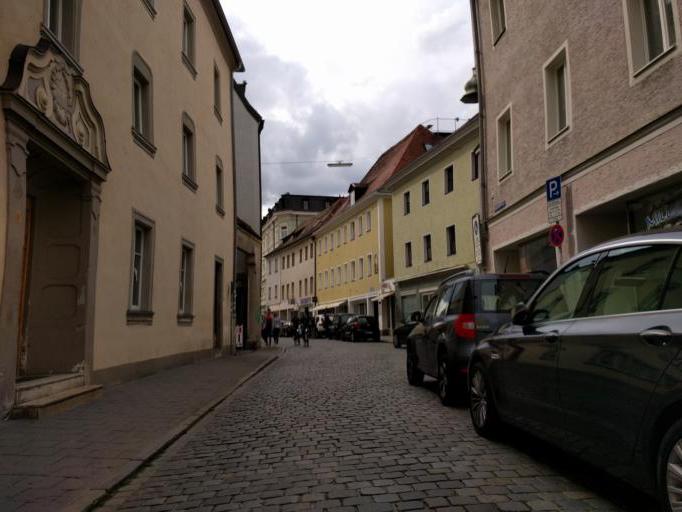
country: DE
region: Bavaria
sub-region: Upper Palatinate
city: Regensburg
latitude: 49.0163
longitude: 12.0973
